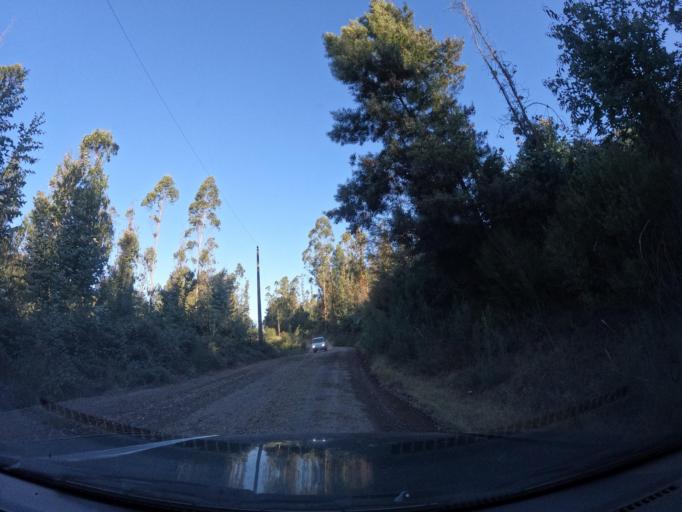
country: CL
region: Biobio
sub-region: Provincia de Concepcion
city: Chiguayante
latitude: -37.0237
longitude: -72.8870
